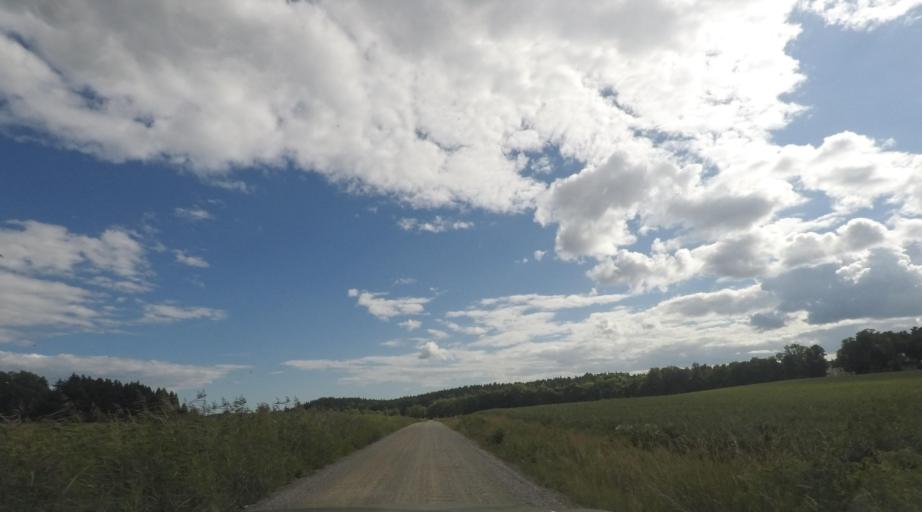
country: SE
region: Stockholm
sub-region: Sodertalje Kommun
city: Pershagen
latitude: 59.1130
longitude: 17.6672
